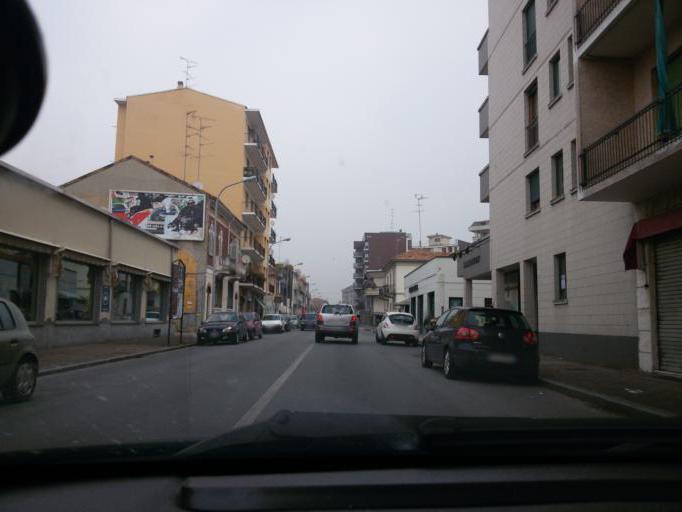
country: IT
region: Piedmont
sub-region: Provincia di Vercelli
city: Vercelli
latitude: 45.3212
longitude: 8.4145
